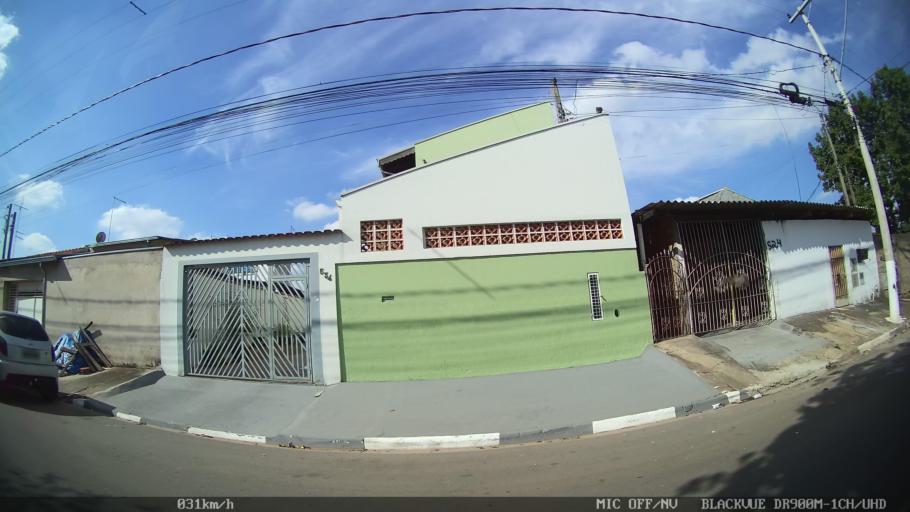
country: BR
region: Sao Paulo
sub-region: Hortolandia
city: Hortolandia
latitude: -22.9005
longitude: -47.2342
